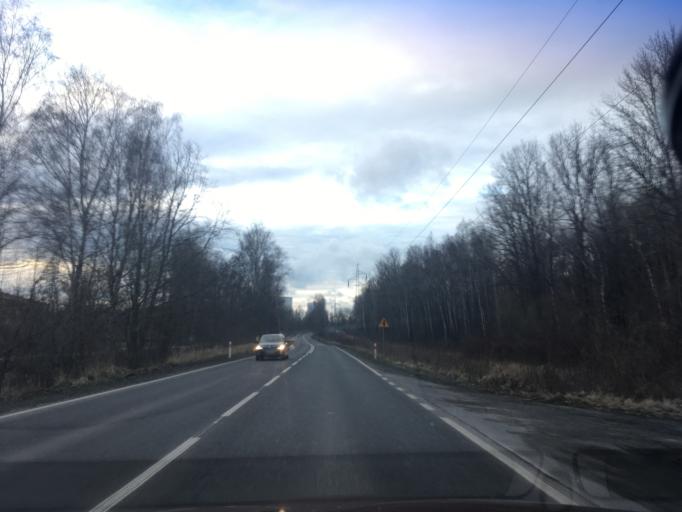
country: DE
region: Saxony
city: Hirschfelde
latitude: 50.9327
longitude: 14.9237
